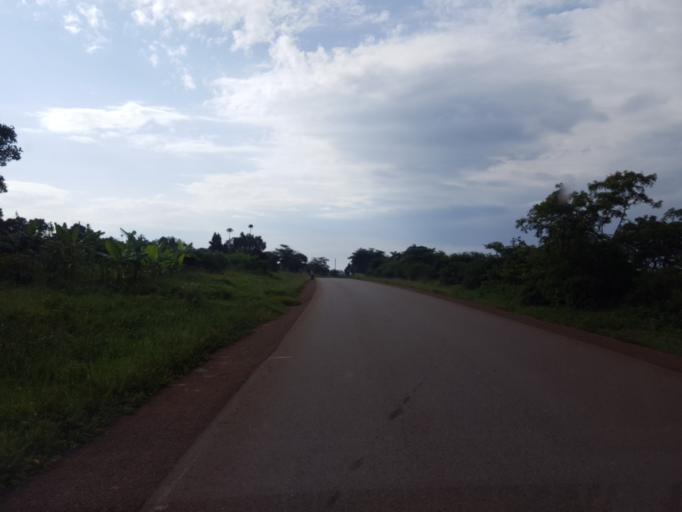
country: UG
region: Western Region
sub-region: Hoima District
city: Hoima
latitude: 1.2544
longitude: 31.5153
